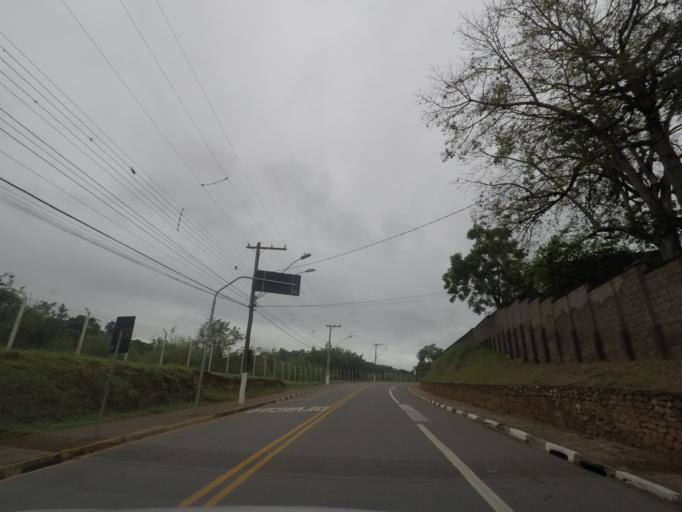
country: BR
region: Sao Paulo
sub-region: Cajati
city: Cajati
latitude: -24.7211
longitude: -48.1017
